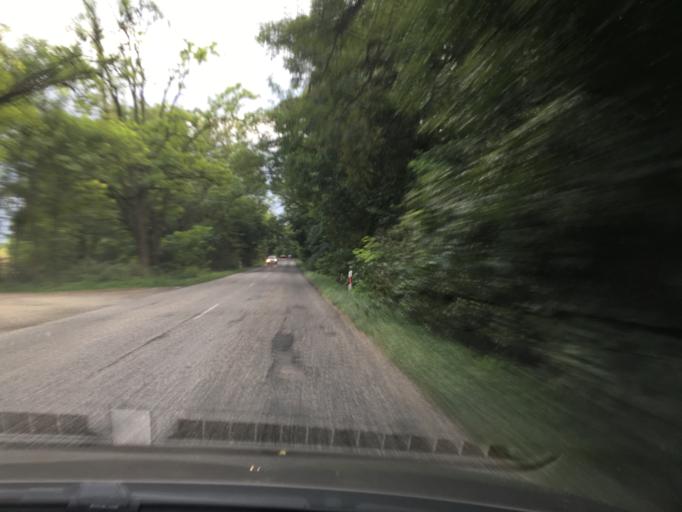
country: HU
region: Pest
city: Szada
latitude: 47.6181
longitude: 19.2997
